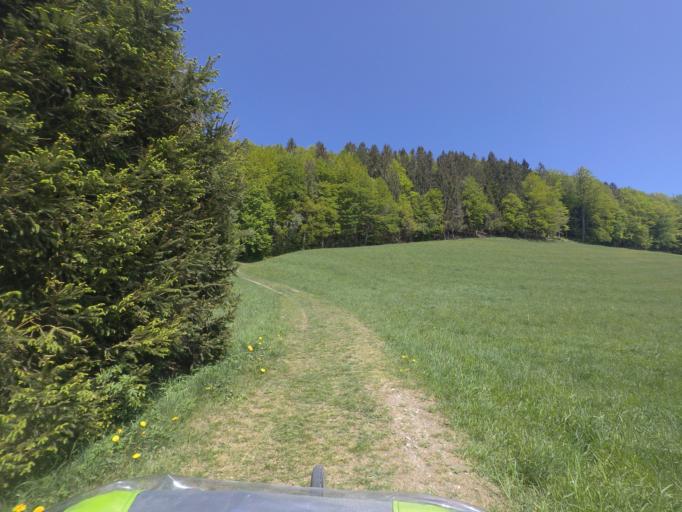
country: AT
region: Salzburg
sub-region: Politischer Bezirk Salzburg-Umgebung
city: Hallwang
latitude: 47.8243
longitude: 13.0918
